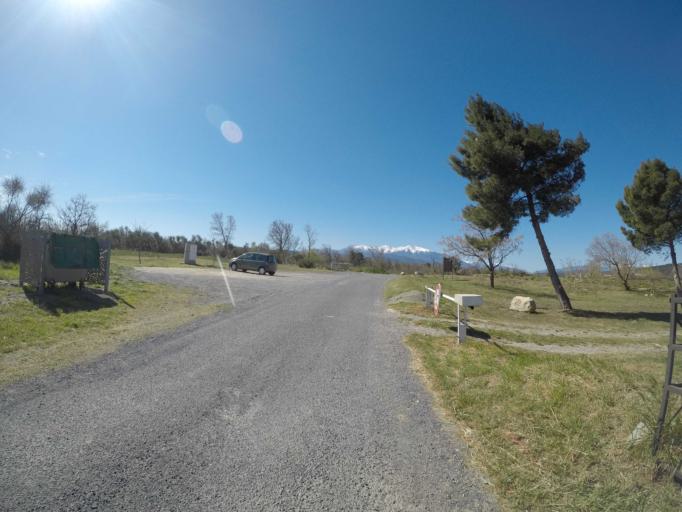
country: FR
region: Languedoc-Roussillon
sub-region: Departement des Pyrenees-Orientales
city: Millas
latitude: 42.6979
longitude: 2.6642
